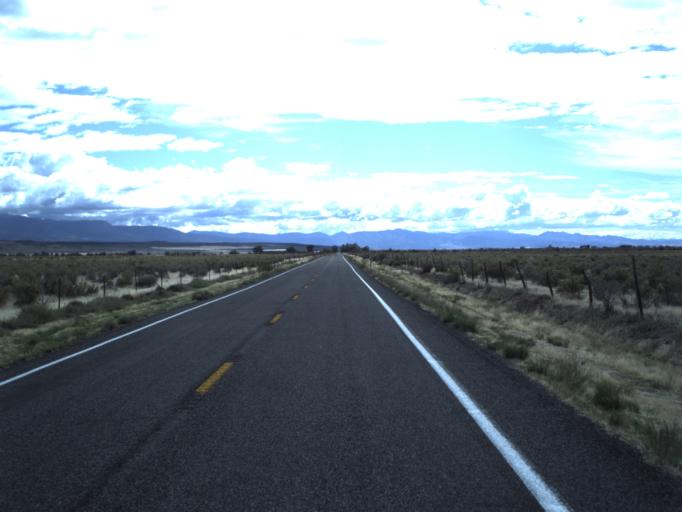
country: US
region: Utah
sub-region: Millard County
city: Fillmore
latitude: 39.0772
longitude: -112.4099
